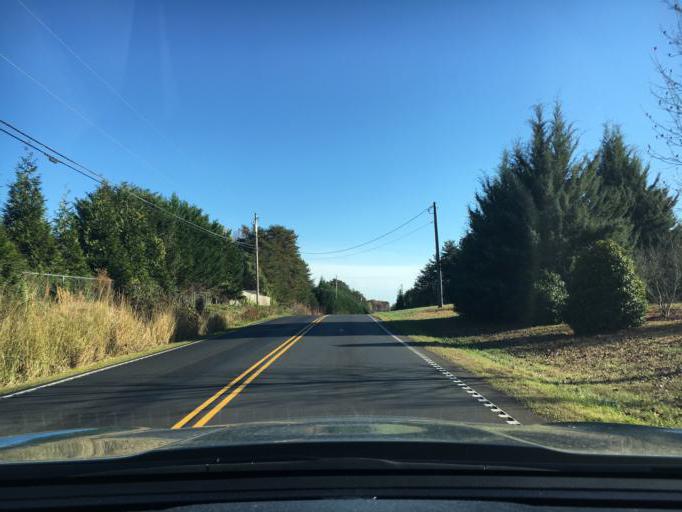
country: US
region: South Carolina
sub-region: Spartanburg County
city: Inman
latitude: 35.0207
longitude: -82.0823
